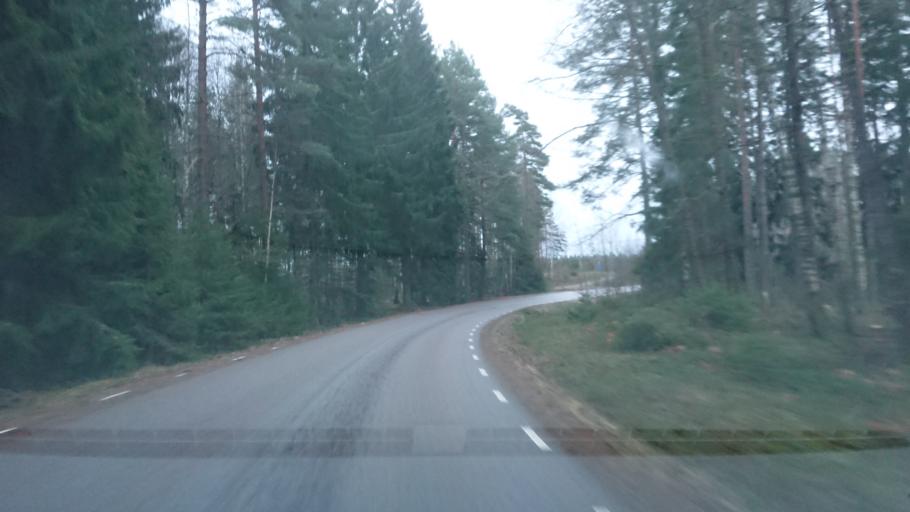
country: SE
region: Uppsala
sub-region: Osthammars Kommun
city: Bjorklinge
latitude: 60.0199
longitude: 17.5780
